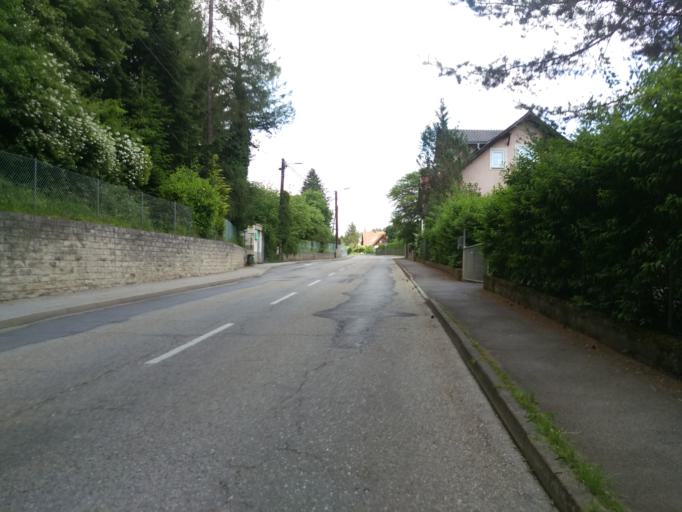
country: AT
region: Styria
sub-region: Graz Stadt
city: Mariatrost
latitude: 47.0885
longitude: 15.4793
